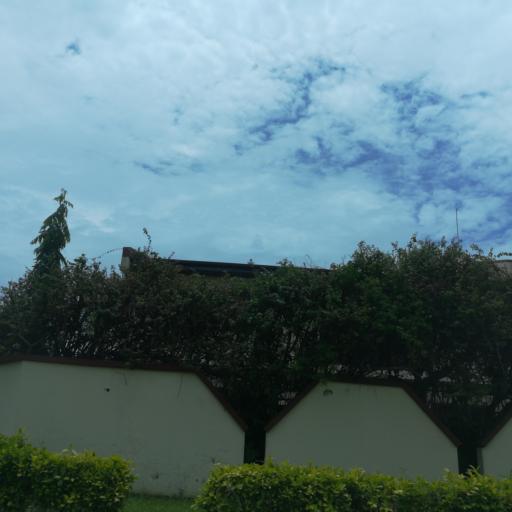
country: NG
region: Lagos
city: Ikoyi
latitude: 6.4426
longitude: 3.4648
